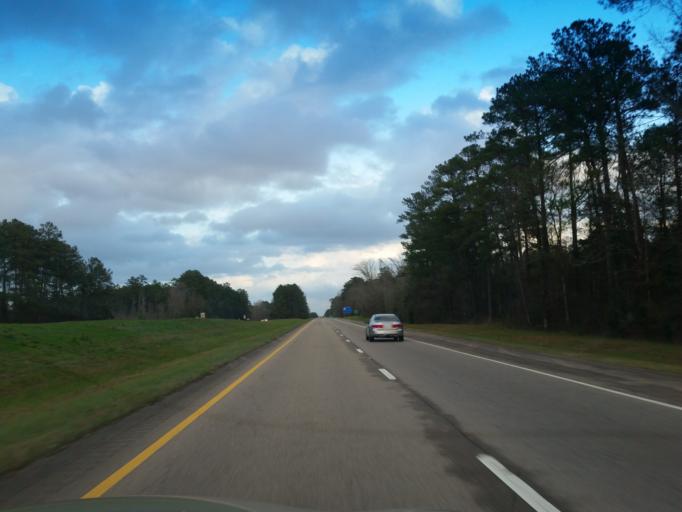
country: US
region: Mississippi
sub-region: Clarke County
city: Stonewall
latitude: 32.0501
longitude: -88.9151
